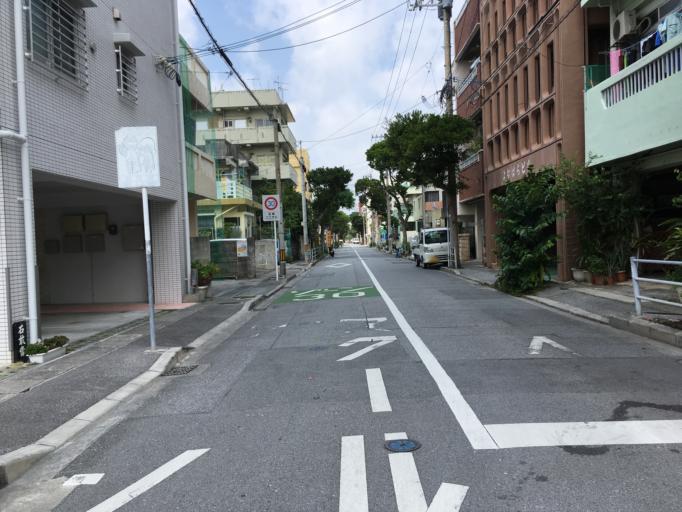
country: JP
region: Okinawa
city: Naha-shi
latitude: 26.2205
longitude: 127.6746
